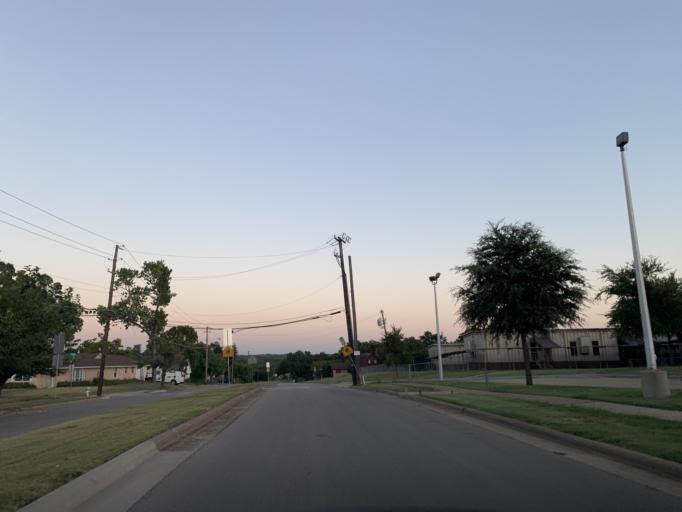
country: US
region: Texas
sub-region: Dallas County
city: Hutchins
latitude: 32.6749
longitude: -96.7971
